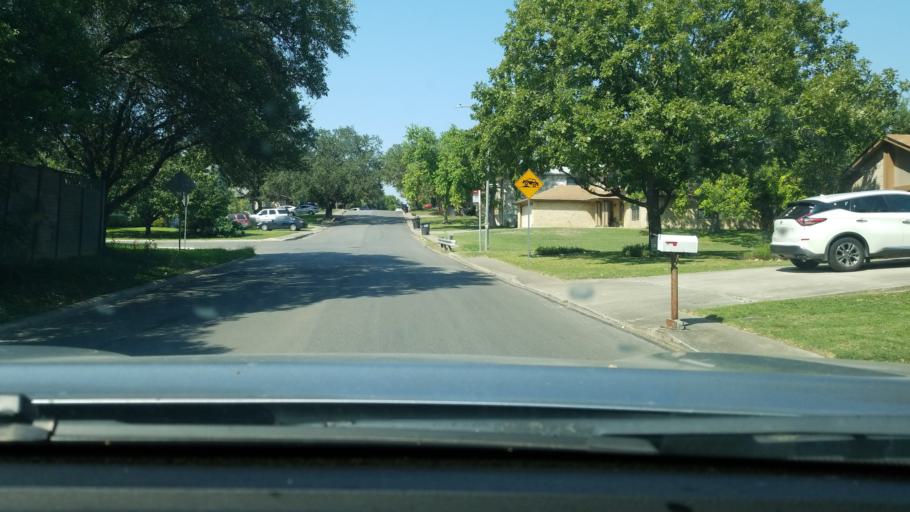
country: US
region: Texas
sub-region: Bexar County
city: Shavano Park
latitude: 29.5588
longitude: -98.6057
